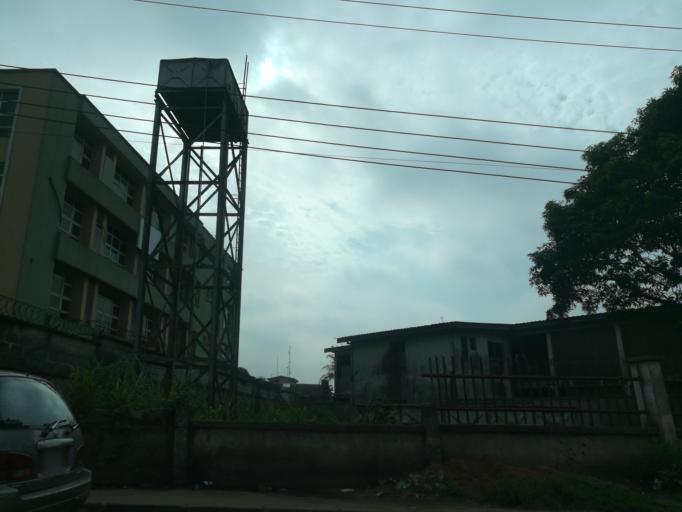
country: NG
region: Rivers
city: Port Harcourt
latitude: 4.8084
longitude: 7.0004
